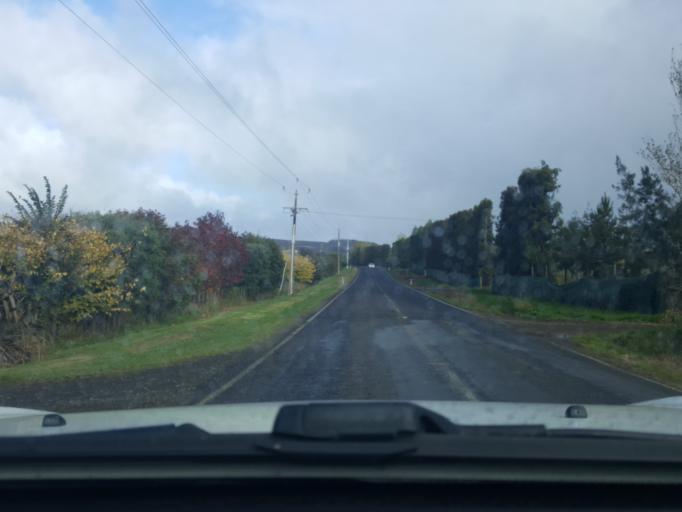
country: NZ
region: Auckland
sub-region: Auckland
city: Pukekohe East
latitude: -37.3031
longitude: 175.0169
